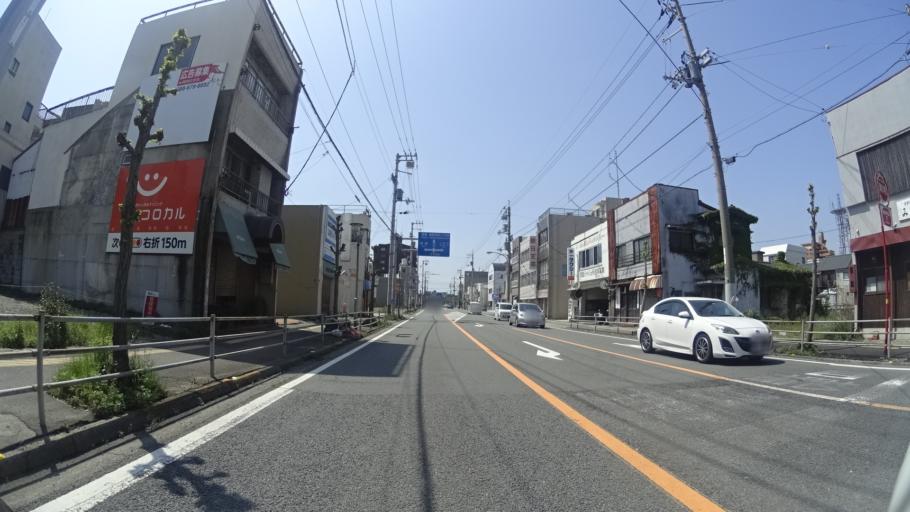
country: JP
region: Tokushima
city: Narutocho-mitsuishi
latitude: 34.1764
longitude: 134.6087
